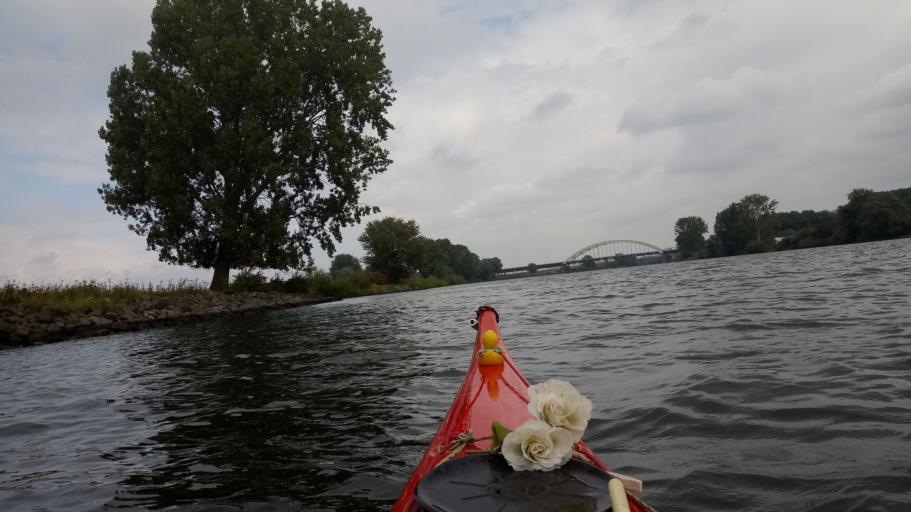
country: NL
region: Gelderland
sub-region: Gemeente Maasdriel
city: Hedel
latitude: 51.7361
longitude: 5.2566
